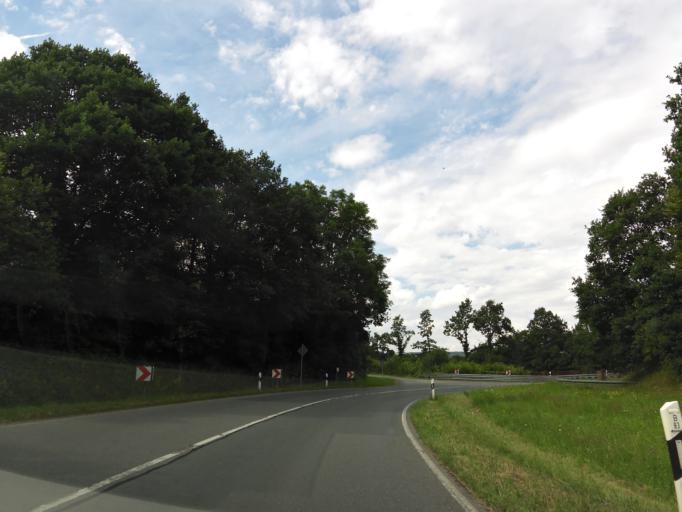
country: DE
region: Lower Saxony
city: Furstenberg
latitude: 51.7136
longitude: 9.3737
